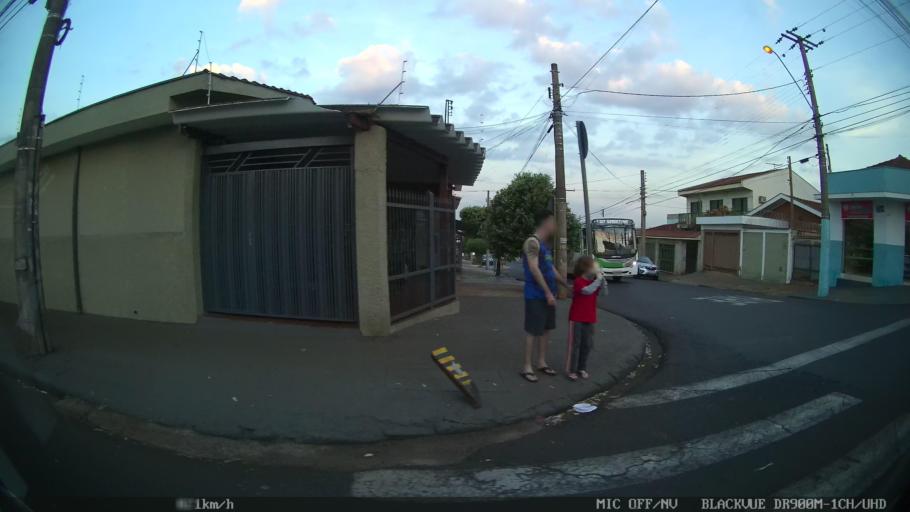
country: BR
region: Sao Paulo
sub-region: Ribeirao Preto
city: Ribeirao Preto
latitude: -21.1546
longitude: -47.8272
